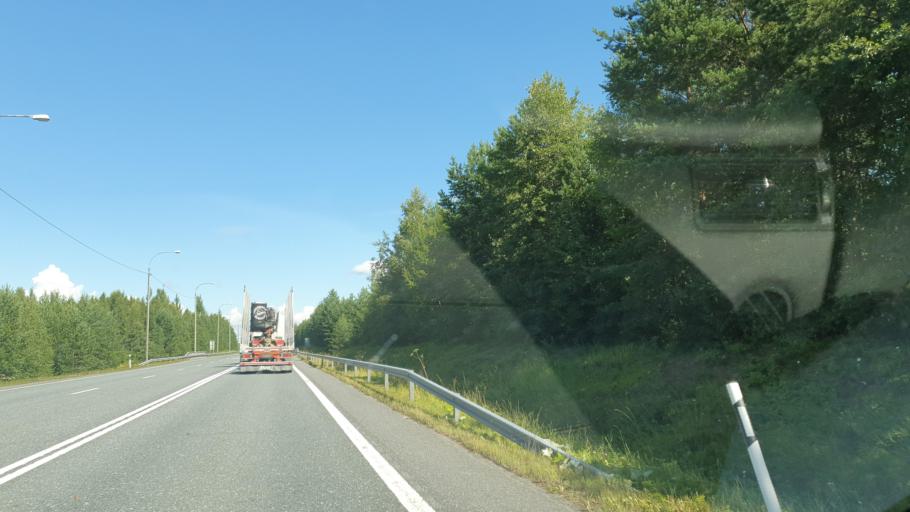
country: FI
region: Northern Savo
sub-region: Ylae-Savo
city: Iisalmi
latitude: 63.6148
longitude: 27.2209
